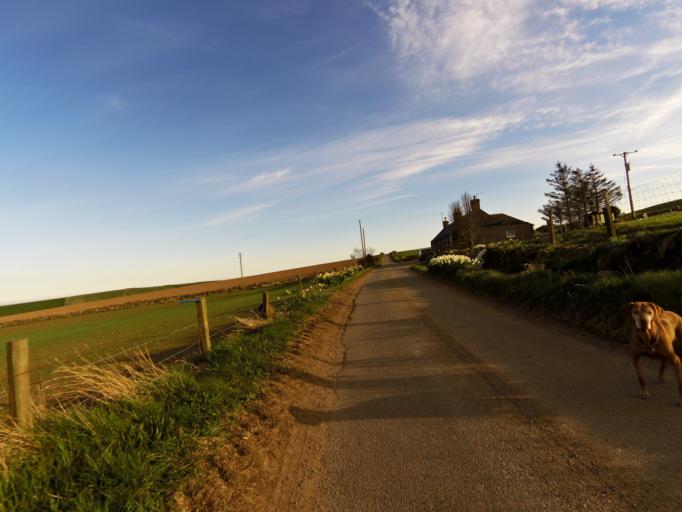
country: GB
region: Scotland
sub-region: Aberdeenshire
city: Inverbervie
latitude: 56.8842
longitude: -2.2370
